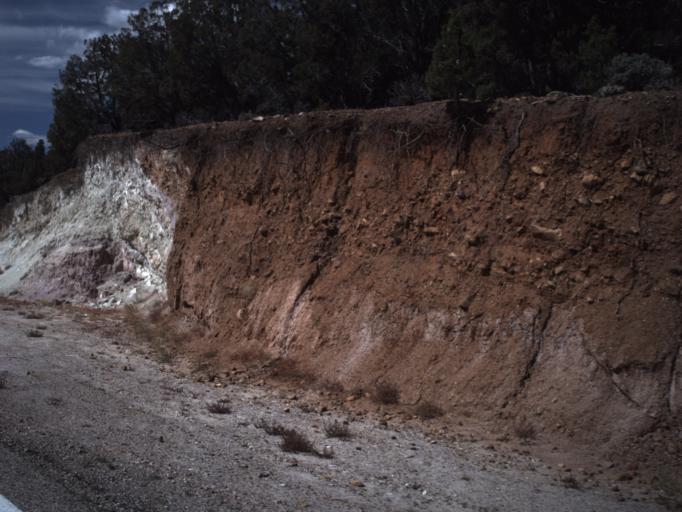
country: US
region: Utah
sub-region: Washington County
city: Enterprise
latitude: 37.5412
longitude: -113.6804
